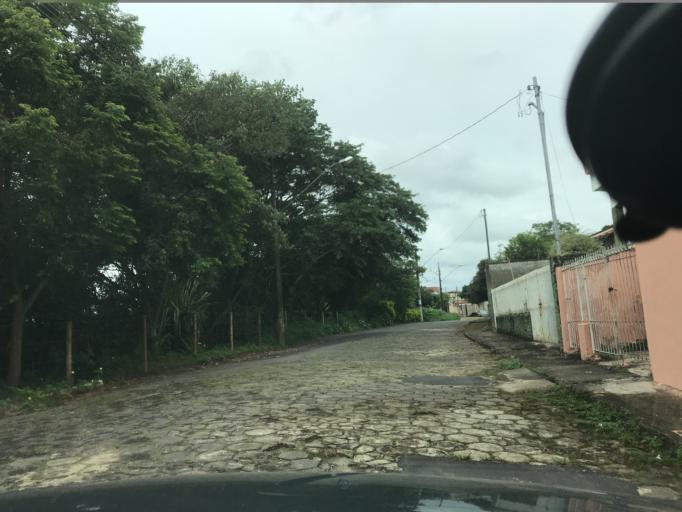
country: BR
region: Minas Gerais
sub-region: Tres Coracoes
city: Tres Coracoes
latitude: -21.7004
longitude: -45.2488
